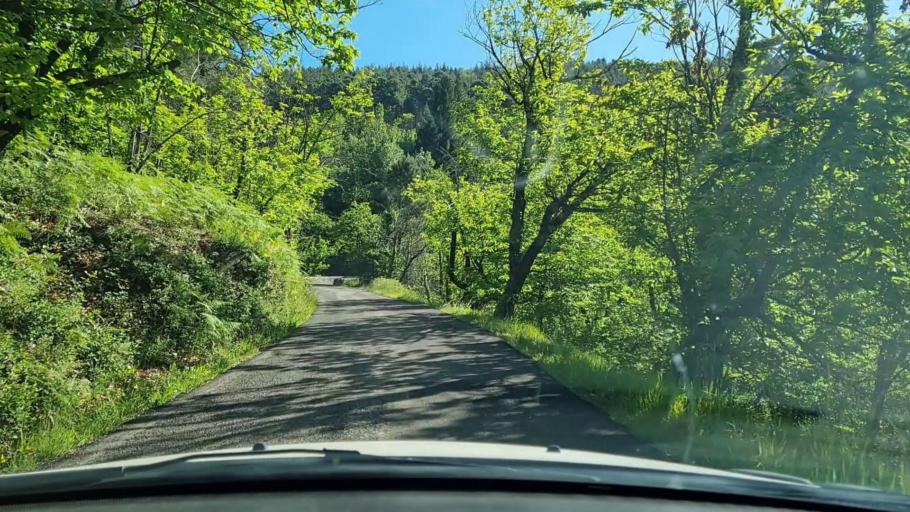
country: FR
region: Languedoc-Roussillon
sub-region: Departement du Gard
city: Branoux-les-Taillades
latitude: 44.1924
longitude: 3.9747
